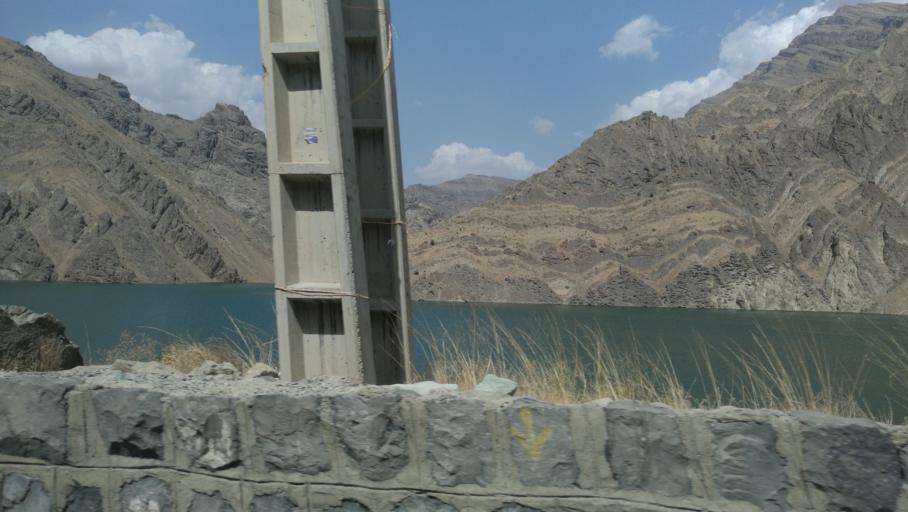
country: IR
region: Alborz
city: Karaj
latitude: 35.9758
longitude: 51.0971
